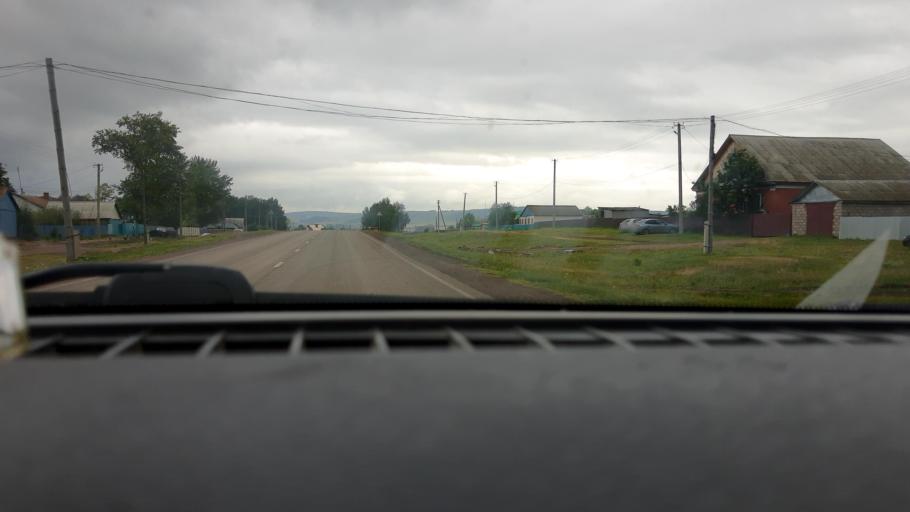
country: RU
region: Bashkortostan
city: Serafimovskiy
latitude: 54.4447
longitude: 53.9758
